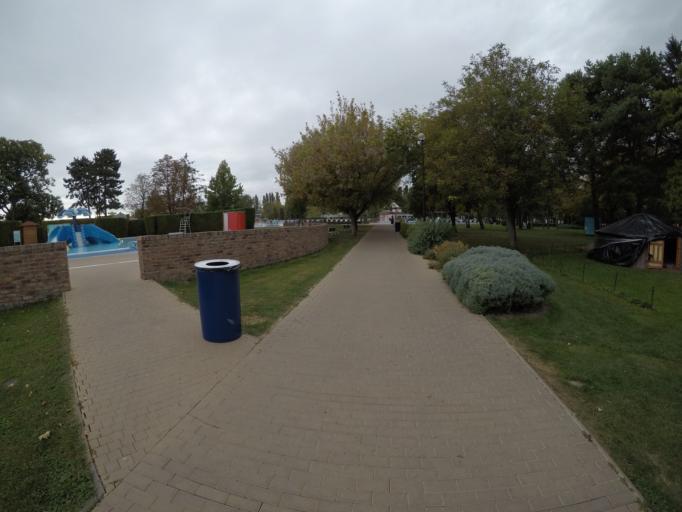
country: SK
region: Trnavsky
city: Dunajska Streda
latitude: 47.9847
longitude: 17.6078
